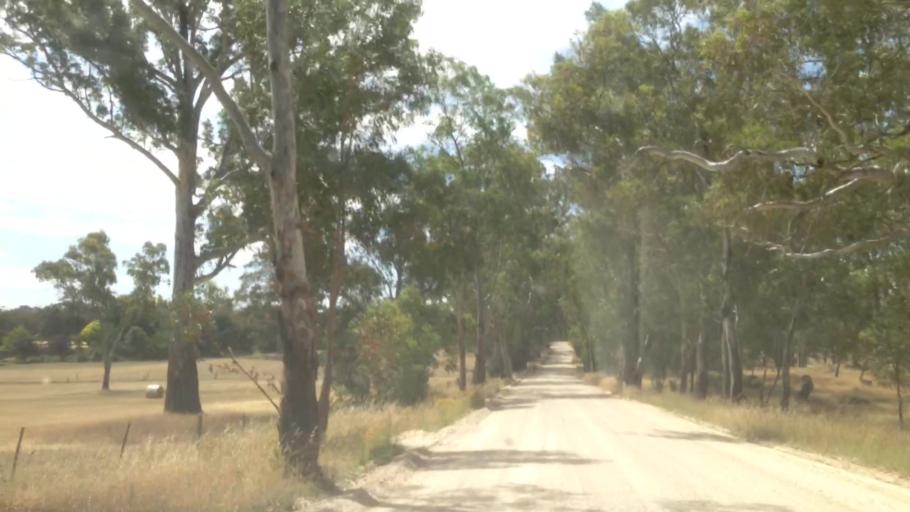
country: AU
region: South Australia
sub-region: Barossa
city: Williamstown
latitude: -34.7206
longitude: 138.9610
